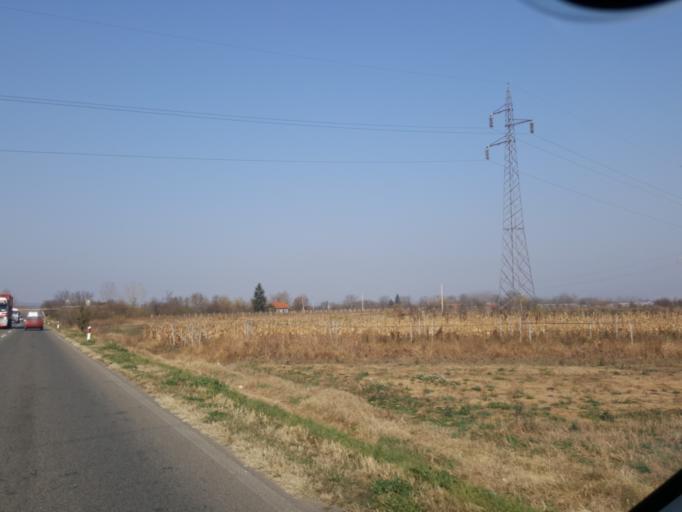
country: RS
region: Central Serbia
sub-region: Jablanicki Okrug
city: Leskovac
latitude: 43.0158
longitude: 21.9551
